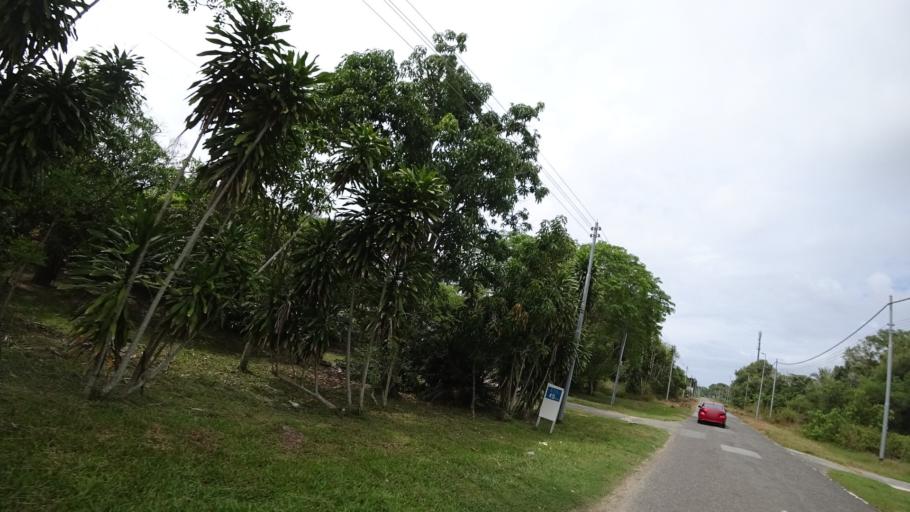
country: BN
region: Tutong
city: Tutong
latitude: 4.7951
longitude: 114.6248
